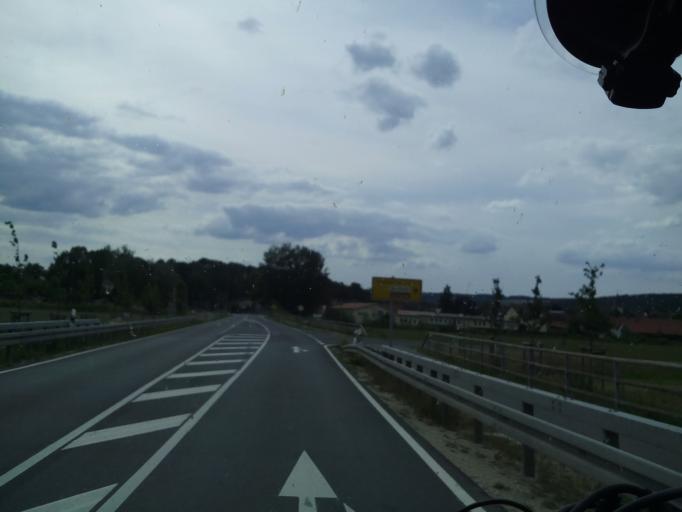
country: DE
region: Bavaria
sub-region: Regierungsbezirk Unterfranken
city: Untermerzbach
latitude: 50.1242
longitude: 10.8641
